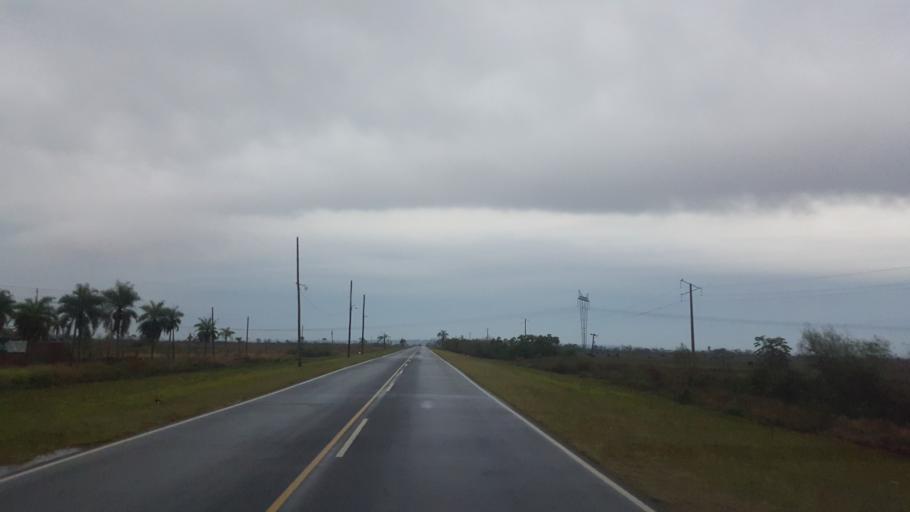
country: AR
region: Corrientes
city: Ituzaingo
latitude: -27.5652
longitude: -56.6613
